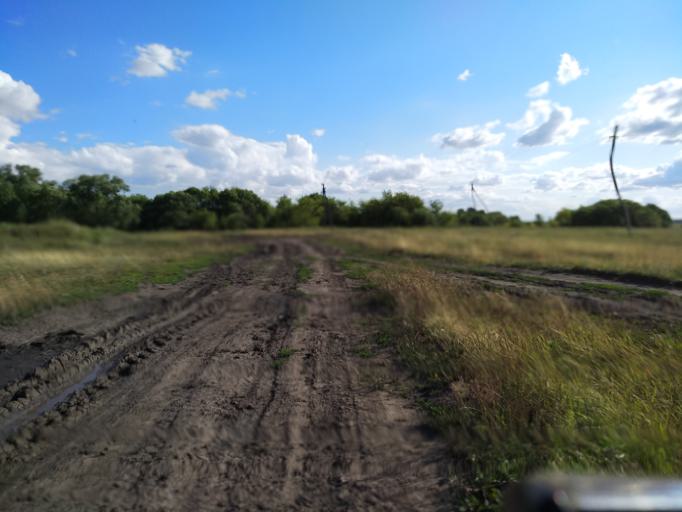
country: RU
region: Lipetsk
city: Dobrinka
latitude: 52.0265
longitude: 40.5607
